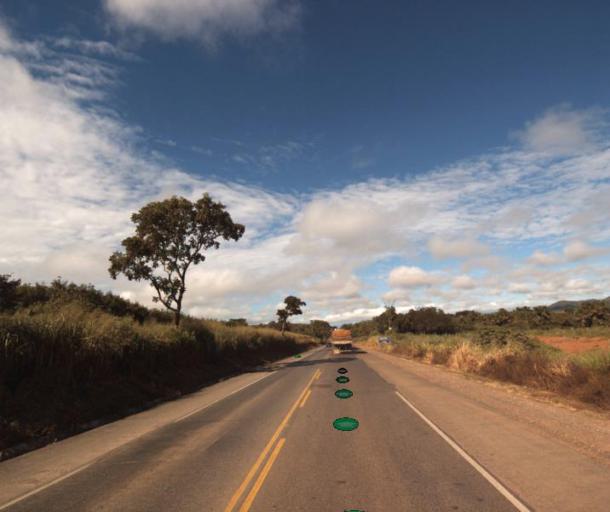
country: BR
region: Goias
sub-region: Uruacu
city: Uruacu
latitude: -14.6377
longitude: -49.1781
